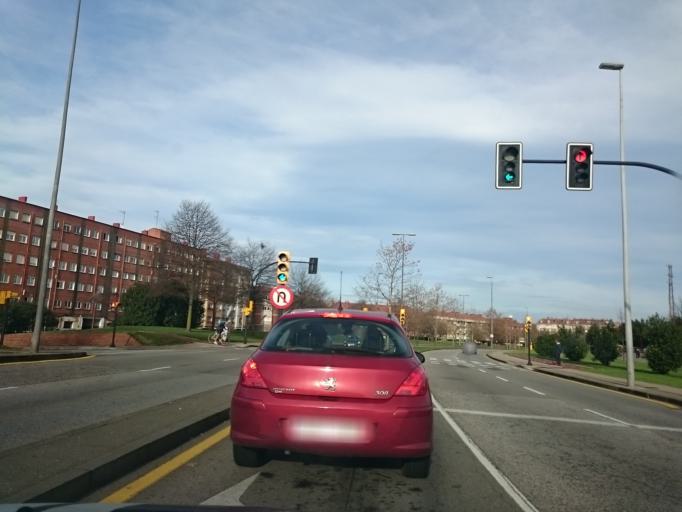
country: ES
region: Asturias
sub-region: Province of Asturias
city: Gijon
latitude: 43.5186
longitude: -5.6569
